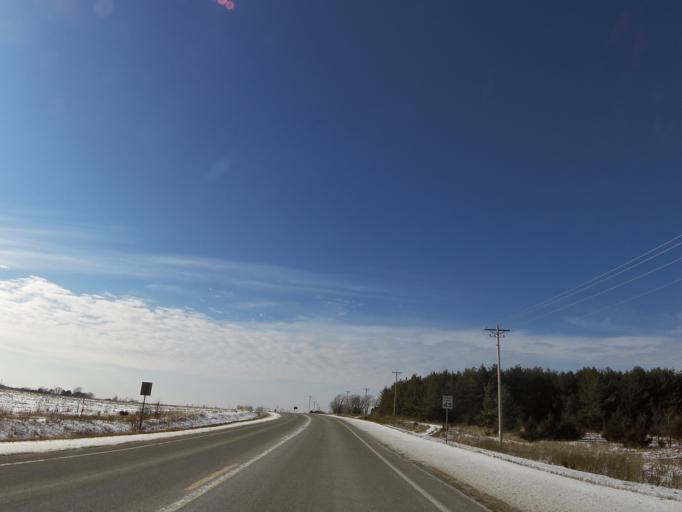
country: US
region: Wisconsin
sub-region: Saint Croix County
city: North Hudson
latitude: 44.9888
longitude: -92.6721
